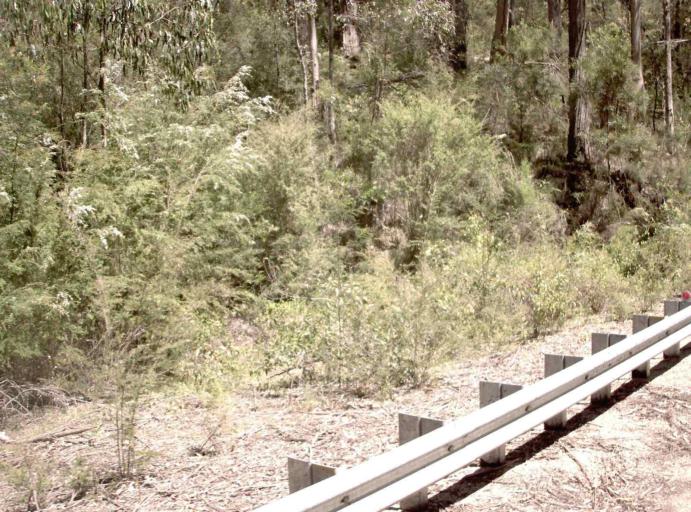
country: AU
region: Victoria
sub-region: East Gippsland
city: Lakes Entrance
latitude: -37.3690
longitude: 148.2188
